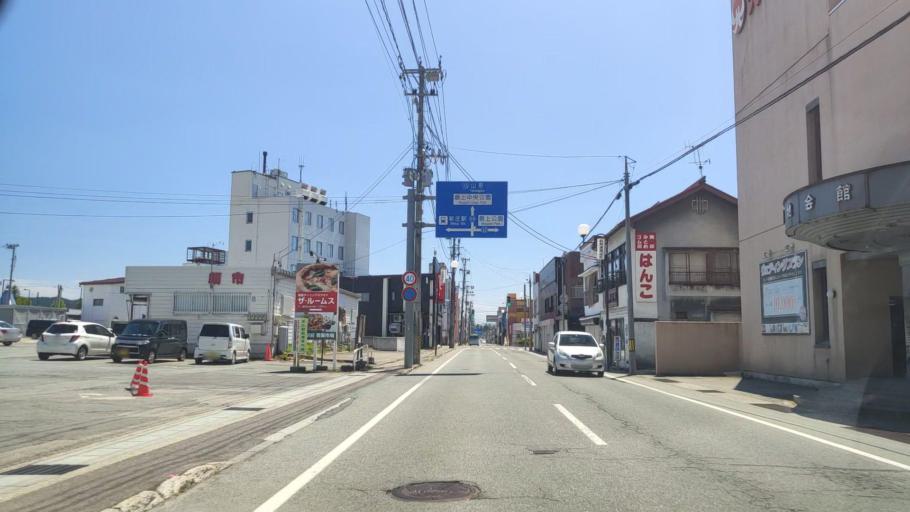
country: JP
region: Yamagata
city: Shinjo
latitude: 38.7636
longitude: 140.3042
